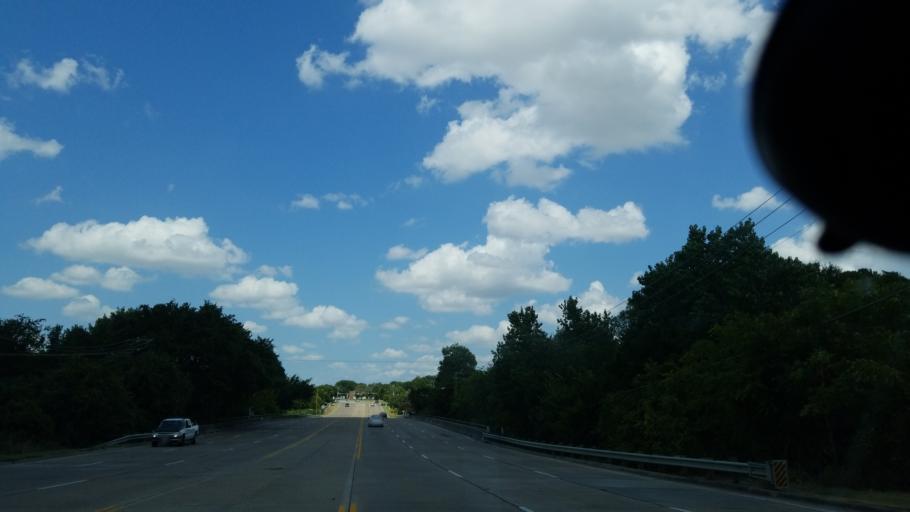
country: US
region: Texas
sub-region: Dallas County
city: Grand Prairie
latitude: 32.7307
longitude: -96.9942
